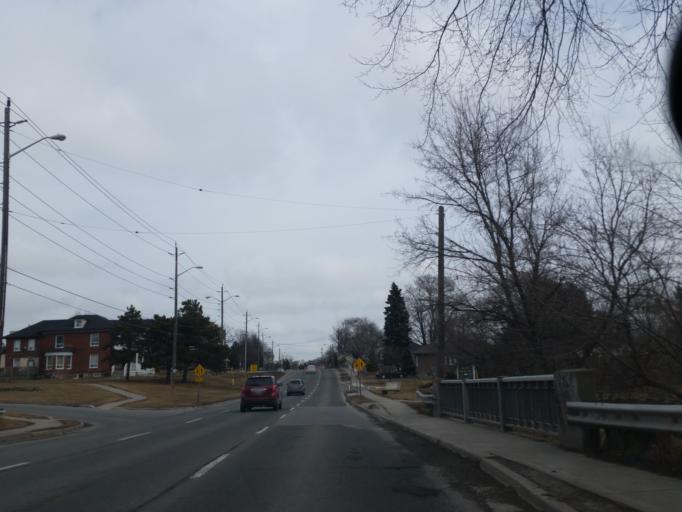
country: CA
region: Ontario
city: Oshawa
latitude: 43.9035
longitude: -78.8380
